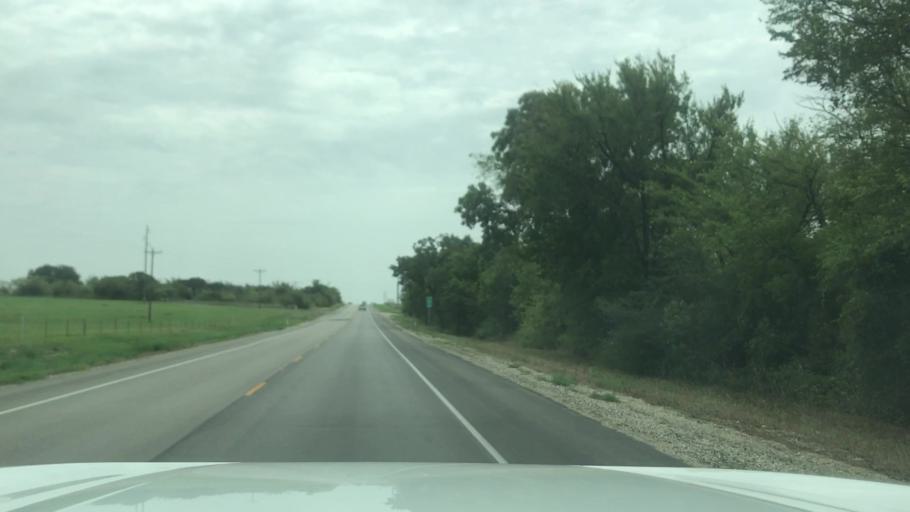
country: US
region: Texas
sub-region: Erath County
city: Dublin
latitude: 32.0888
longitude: -98.2601
